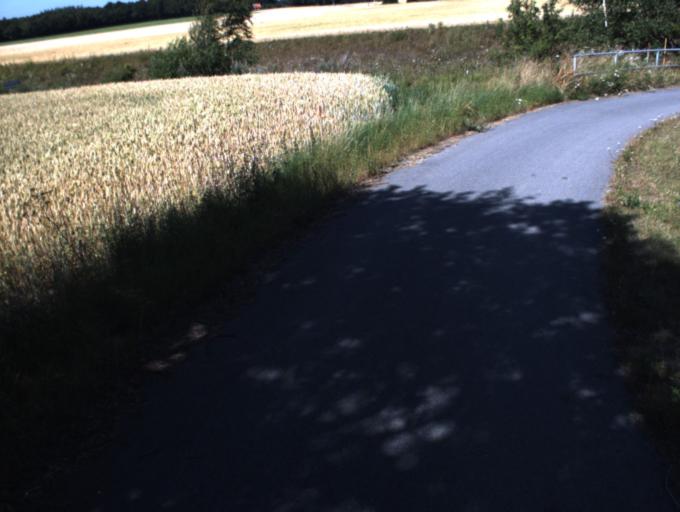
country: SE
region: Skane
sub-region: Helsingborg
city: Odakra
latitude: 56.0826
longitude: 12.7199
